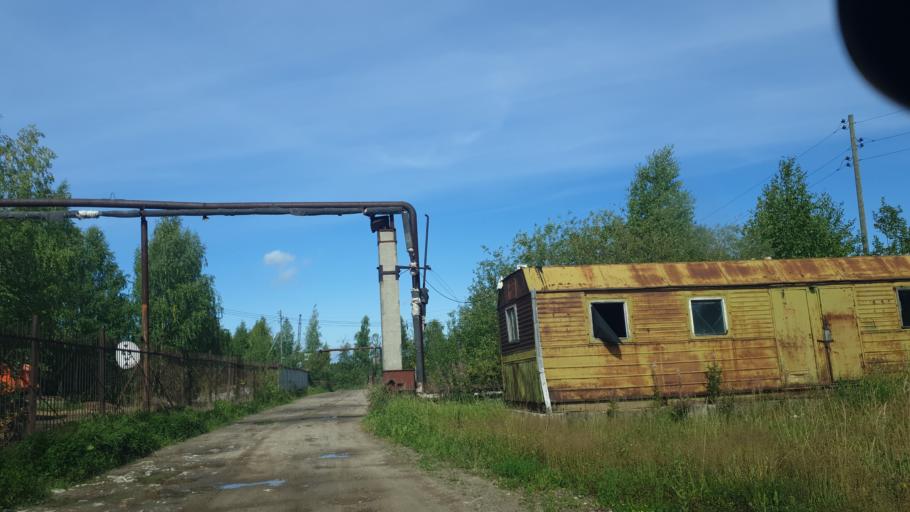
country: RU
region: Komi Republic
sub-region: Syktyvdinskiy Rayon
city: Syktyvkar
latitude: 61.7239
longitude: 50.7526
